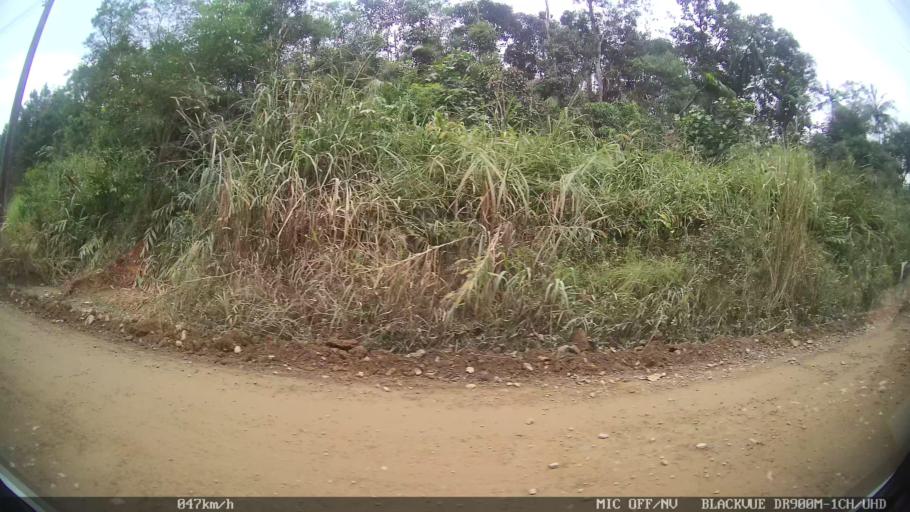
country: BR
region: Santa Catarina
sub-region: Joinville
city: Joinville
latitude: -26.2421
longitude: -48.9255
